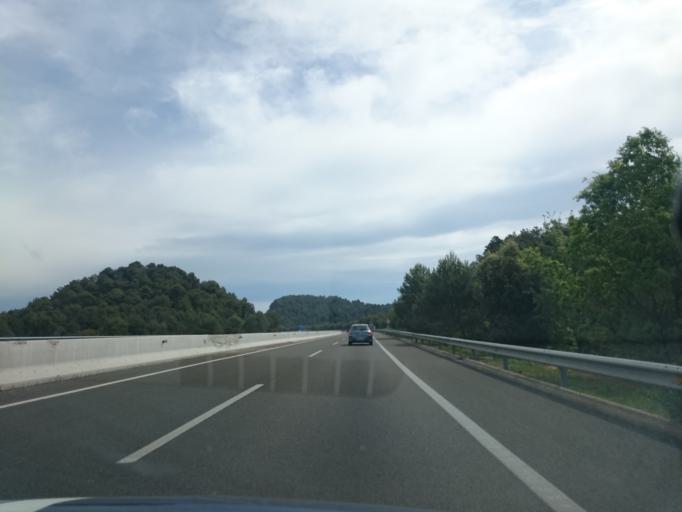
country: ES
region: Catalonia
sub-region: Provincia de Barcelona
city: Orista
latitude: 41.8938
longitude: 2.0701
